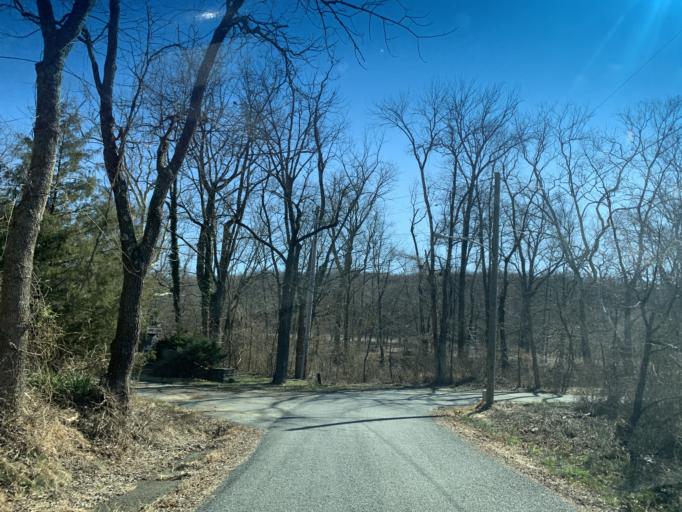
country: US
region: Maryland
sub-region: Harford County
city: Aberdeen
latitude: 39.6195
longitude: -76.2343
